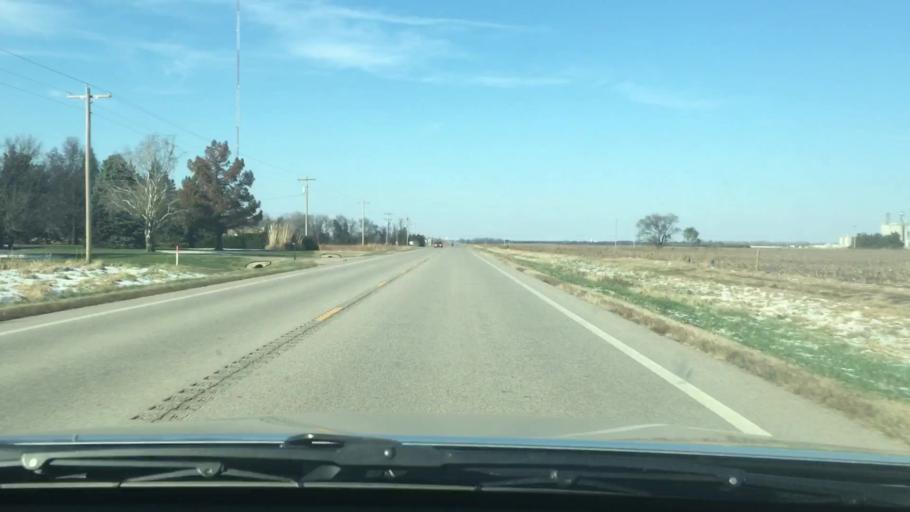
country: US
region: Kansas
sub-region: Rice County
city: Sterling
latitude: 38.2724
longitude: -98.2020
